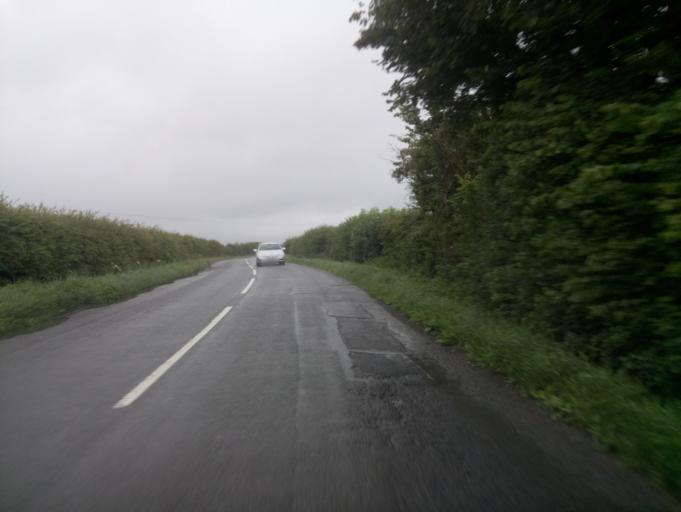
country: GB
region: England
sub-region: Gloucestershire
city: Uckington
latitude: 51.9224
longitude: -2.1386
